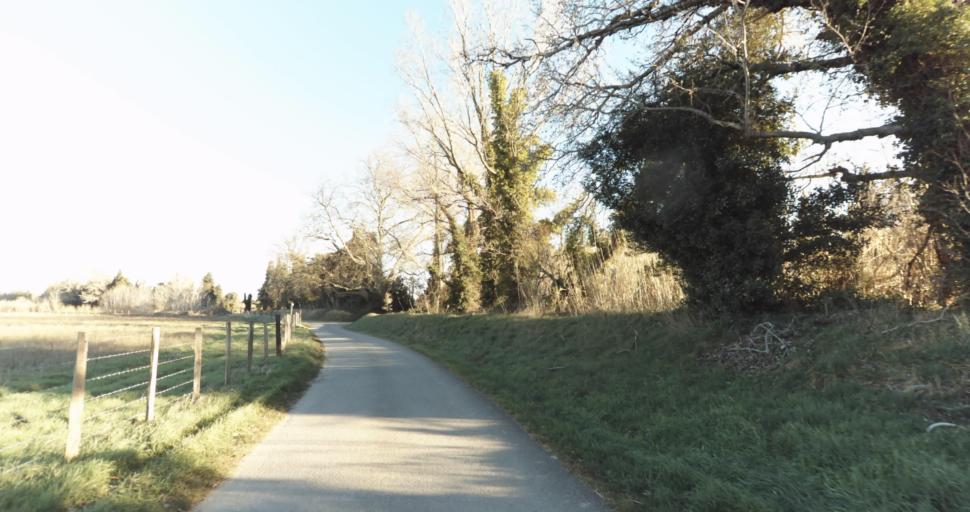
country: FR
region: Provence-Alpes-Cote d'Azur
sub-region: Departement des Bouches-du-Rhone
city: Barbentane
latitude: 43.9151
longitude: 4.7552
